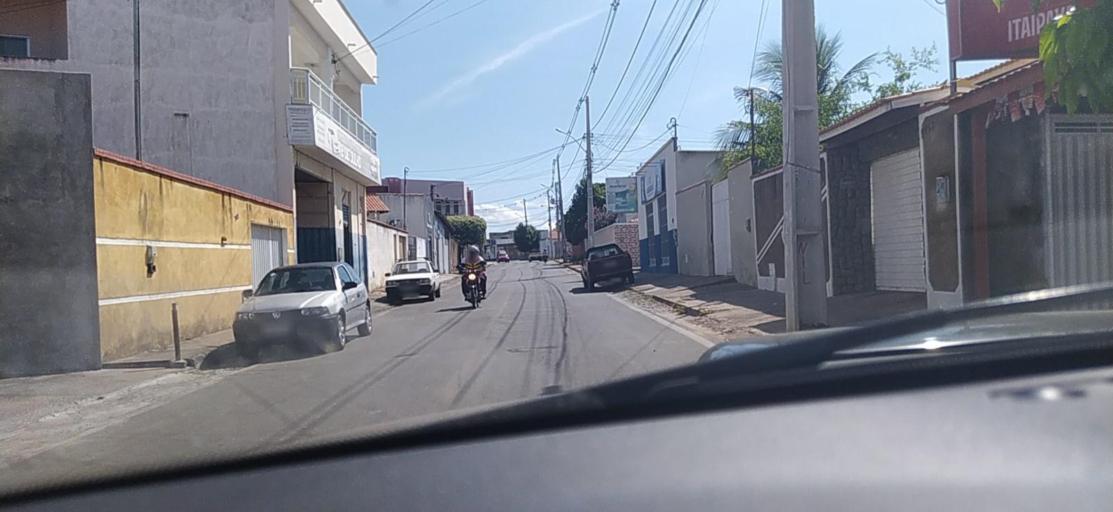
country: BR
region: Bahia
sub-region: Guanambi
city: Guanambi
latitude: -14.2154
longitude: -42.7681
